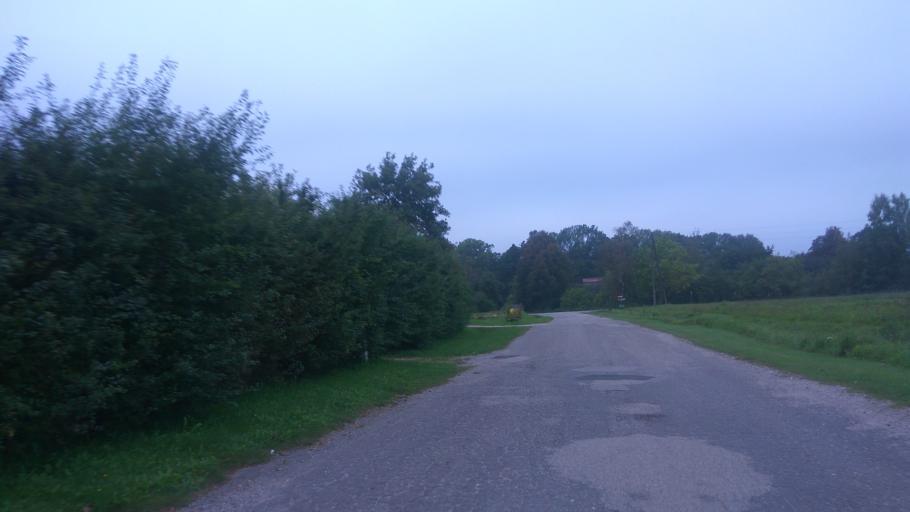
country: LV
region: Rucavas
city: Rucava
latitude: 56.1565
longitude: 21.1690
